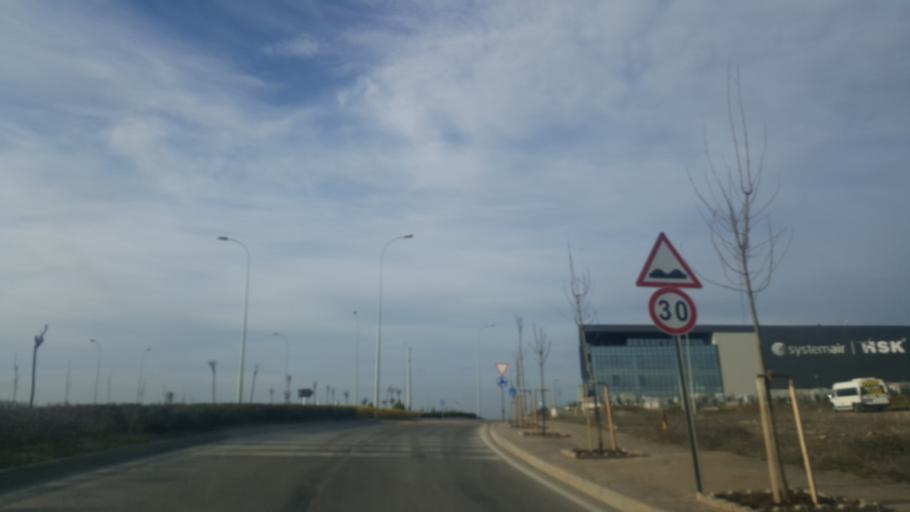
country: TR
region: Kocaeli
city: Tavsanli
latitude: 40.8347
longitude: 29.5499
